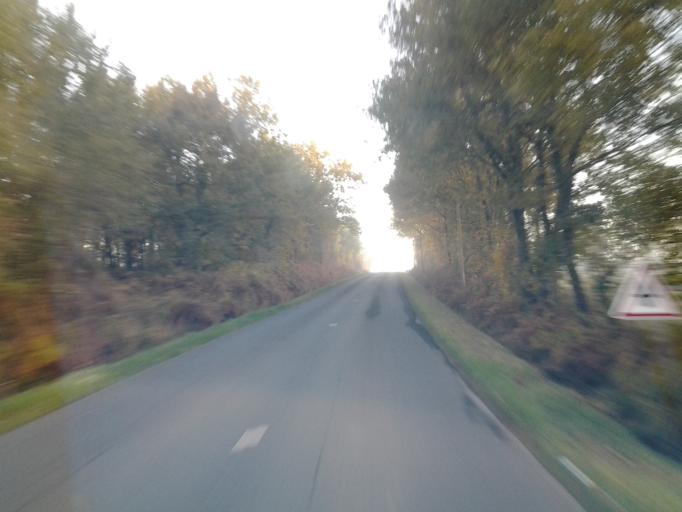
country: FR
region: Pays de la Loire
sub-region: Departement de la Vendee
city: Chateau-Guibert
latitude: 46.6389
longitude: -1.2331
